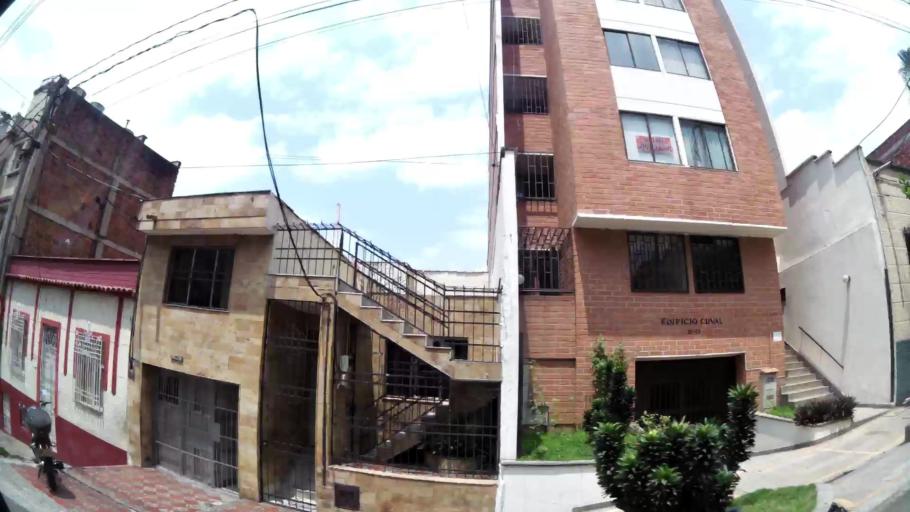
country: CO
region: Antioquia
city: Medellin
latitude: 6.2538
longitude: -75.5590
